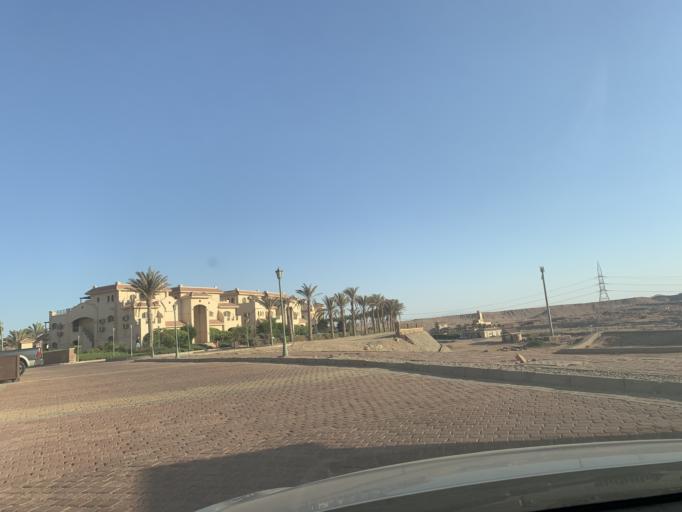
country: EG
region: As Suways
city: Ain Sukhna
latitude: 29.3744
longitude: 32.5685
